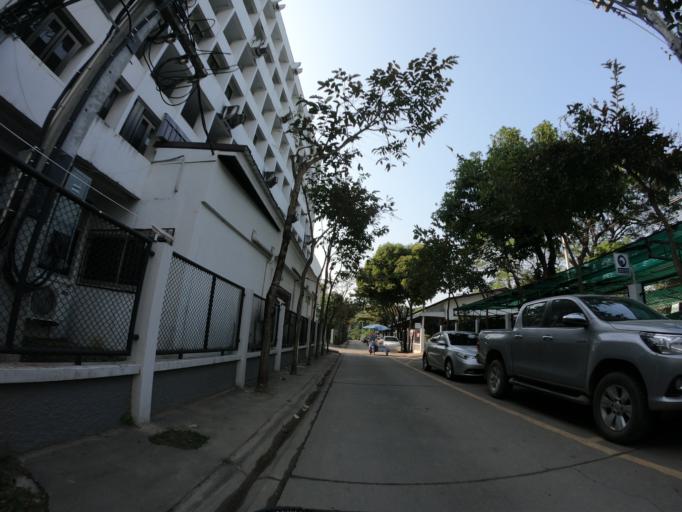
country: TH
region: Chiang Mai
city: Chiang Mai
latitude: 18.7740
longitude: 99.0067
